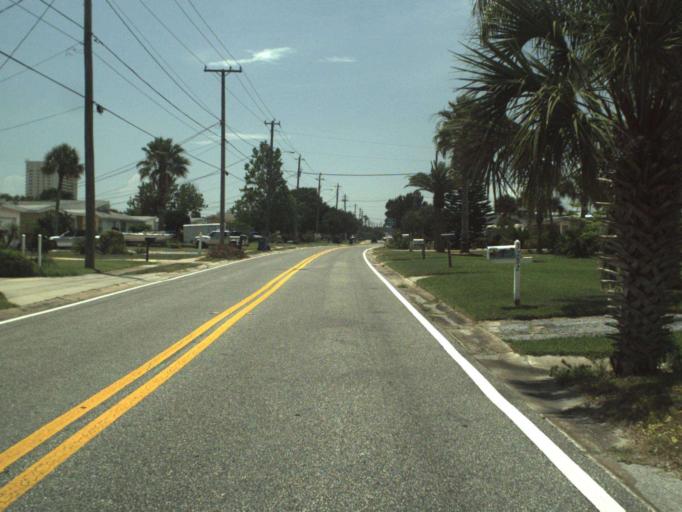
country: US
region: Florida
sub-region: Volusia County
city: Daytona Beach Shores
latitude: 29.1574
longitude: -80.9757
